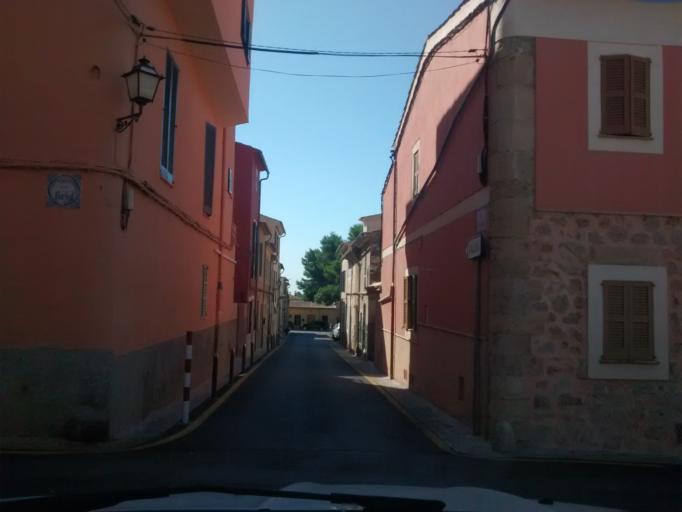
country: ES
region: Balearic Islands
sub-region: Illes Balears
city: Alaro
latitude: 39.7041
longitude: 2.7894
